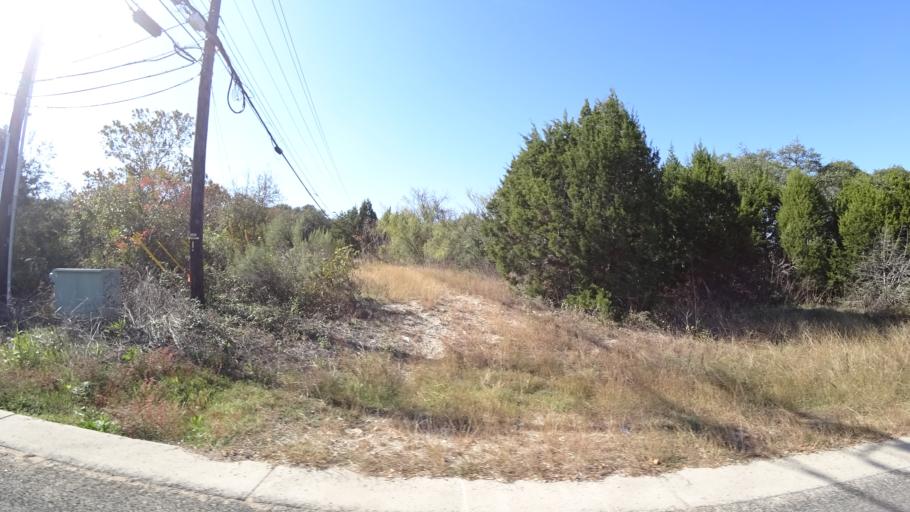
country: US
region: Texas
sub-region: Travis County
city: Barton Creek
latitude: 30.2325
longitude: -97.8751
